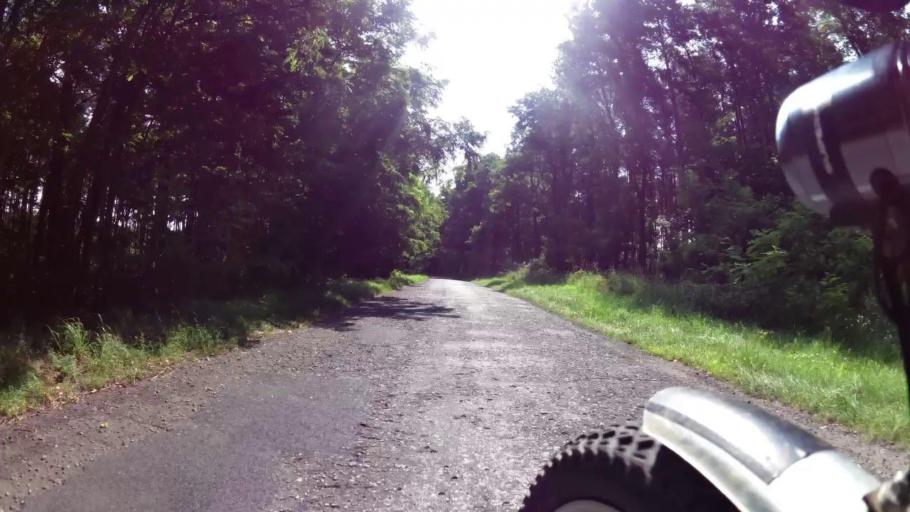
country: DE
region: Brandenburg
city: Zechin
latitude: 52.6759
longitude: 14.4962
